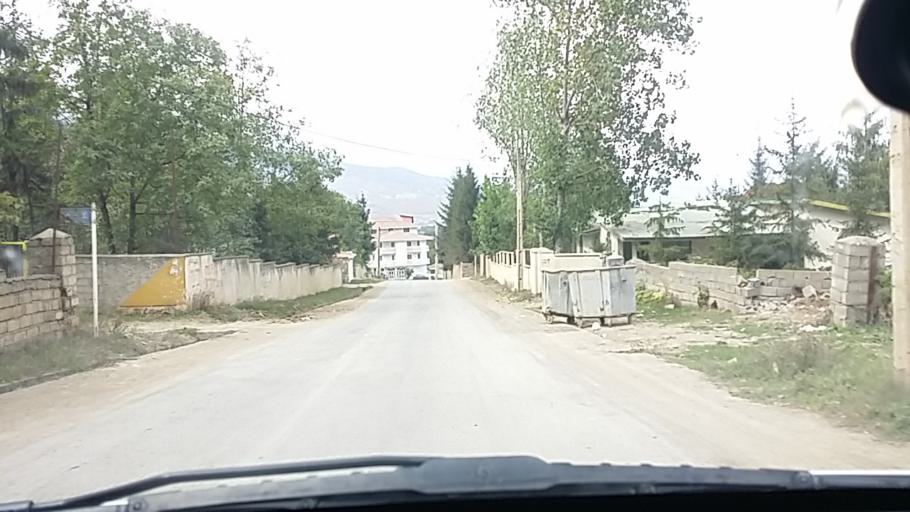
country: IR
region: Mazandaran
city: `Abbasabad
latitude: 36.4952
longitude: 51.1654
